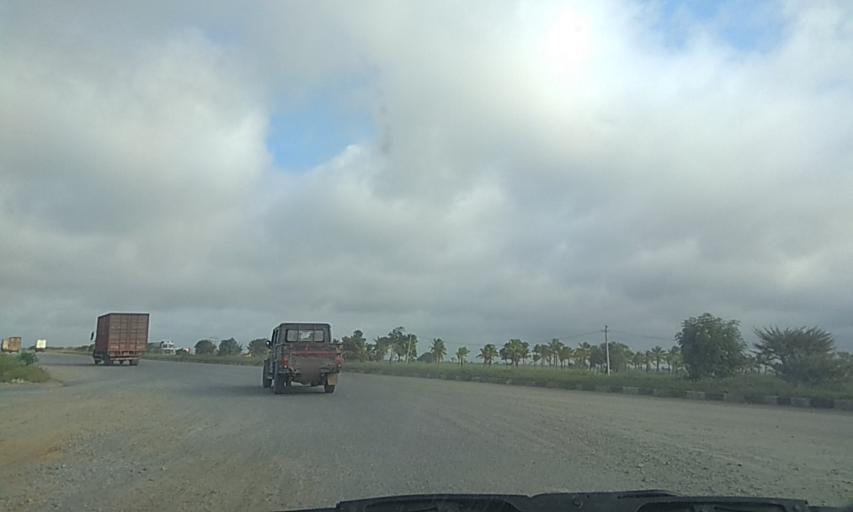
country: IN
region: Karnataka
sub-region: Haveri
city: Savanur
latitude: 14.8864
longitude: 75.3038
